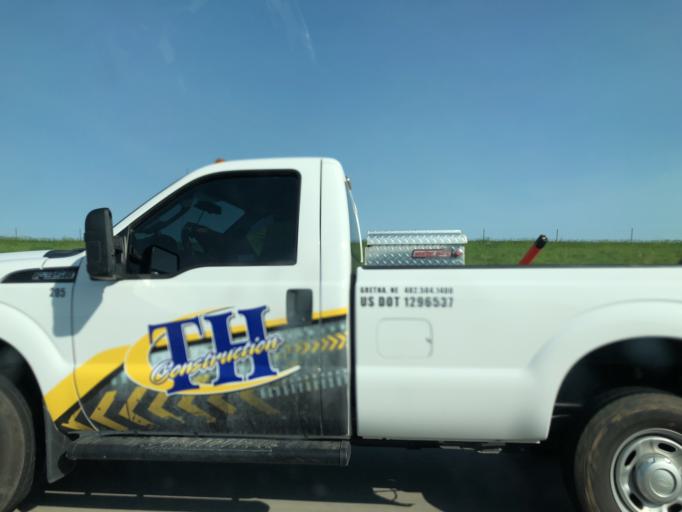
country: US
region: Nebraska
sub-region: Saunders County
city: Ashland
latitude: 40.9643
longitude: -96.3999
